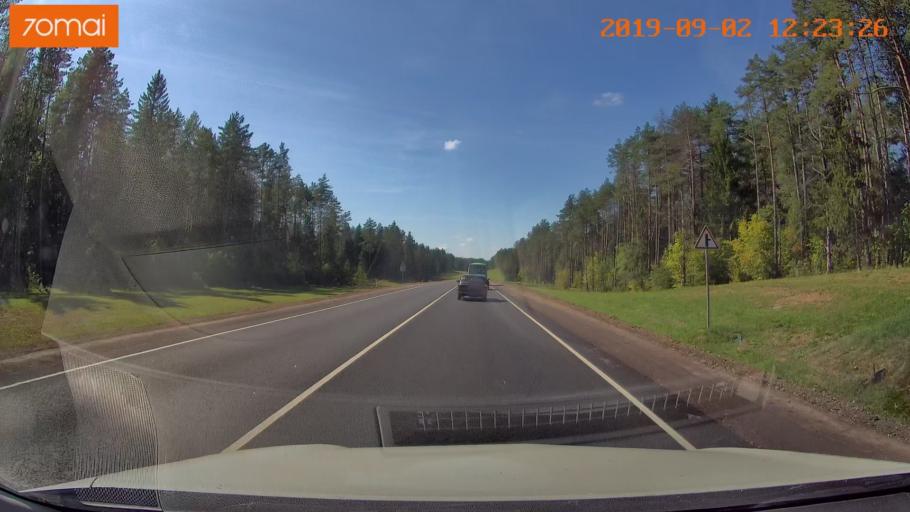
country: RU
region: Smolensk
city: Shumyachi
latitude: 53.8743
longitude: 32.6200
